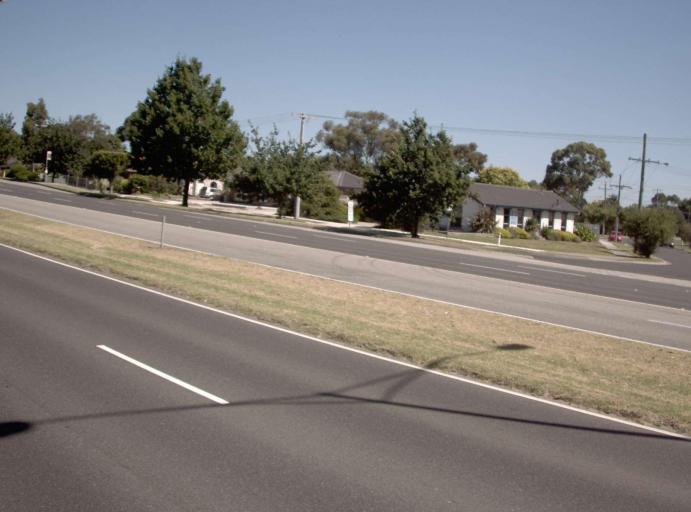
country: AU
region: Victoria
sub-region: Casey
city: Narre Warren
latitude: -38.0206
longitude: 145.2991
